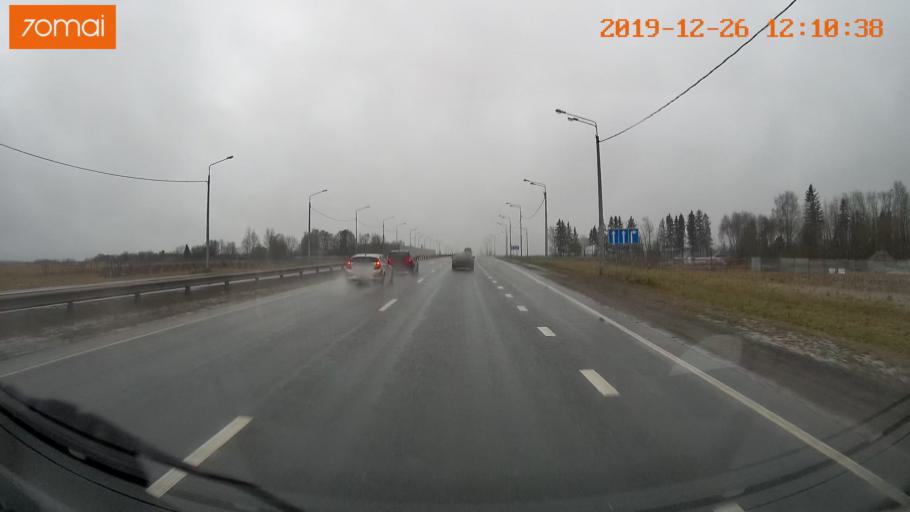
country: RU
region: Vologda
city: Tonshalovo
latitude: 59.2577
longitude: 37.9774
